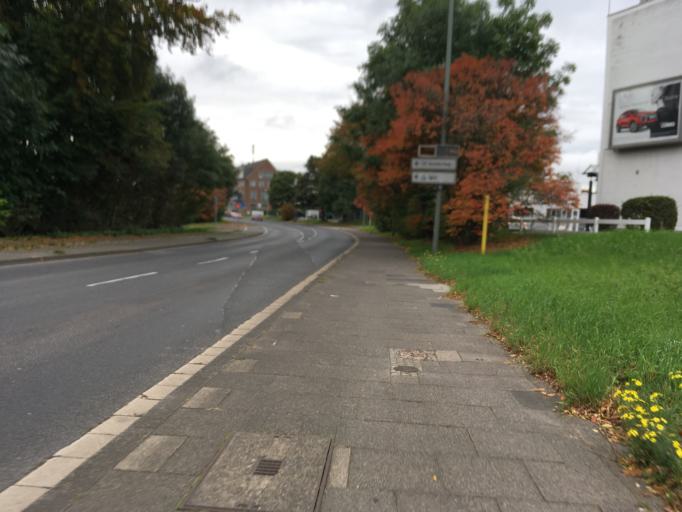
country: DE
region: North Rhine-Westphalia
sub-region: Regierungsbezirk Dusseldorf
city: Neuss
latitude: 51.2023
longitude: 6.7067
